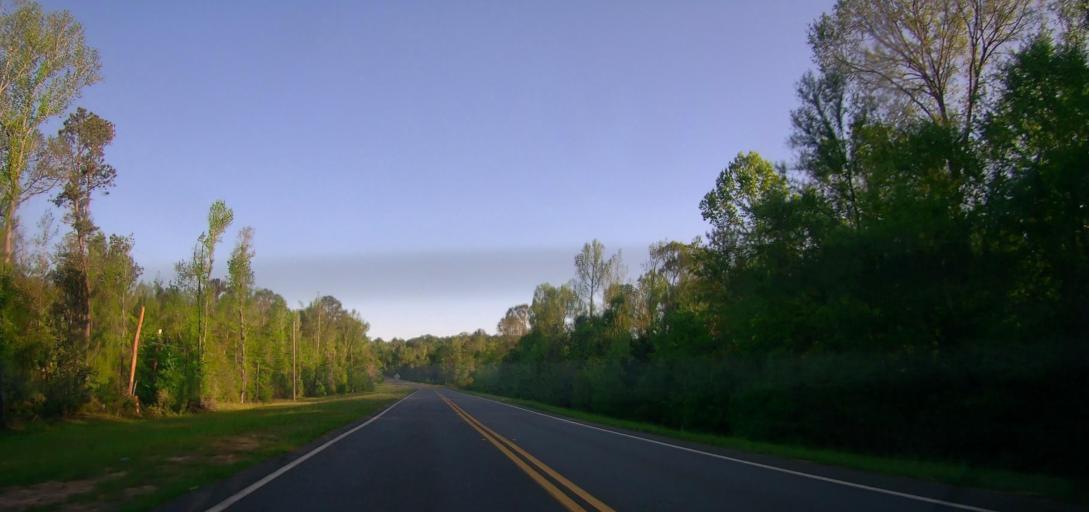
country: US
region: Georgia
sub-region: Macon County
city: Oglethorpe
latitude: 32.3081
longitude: -84.1615
